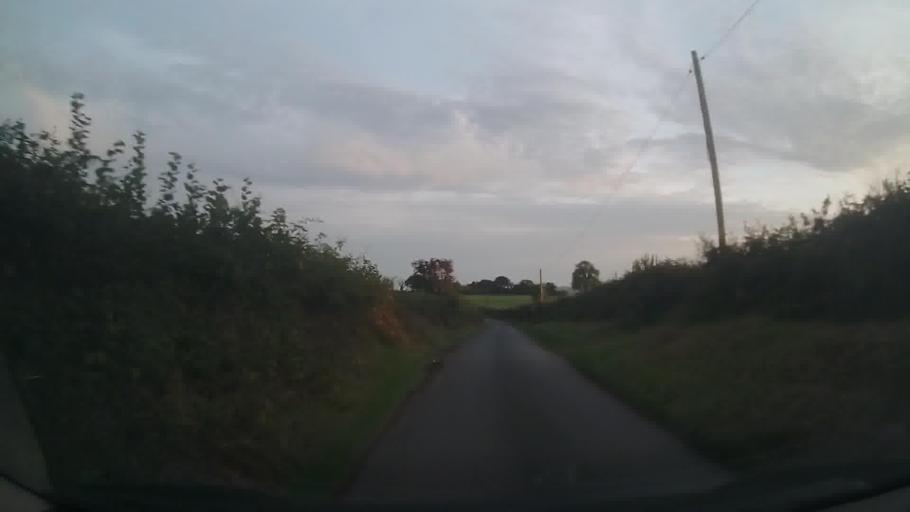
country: GB
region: Wales
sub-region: Pembrokeshire
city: Saundersfoot
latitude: 51.7463
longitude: -4.6592
